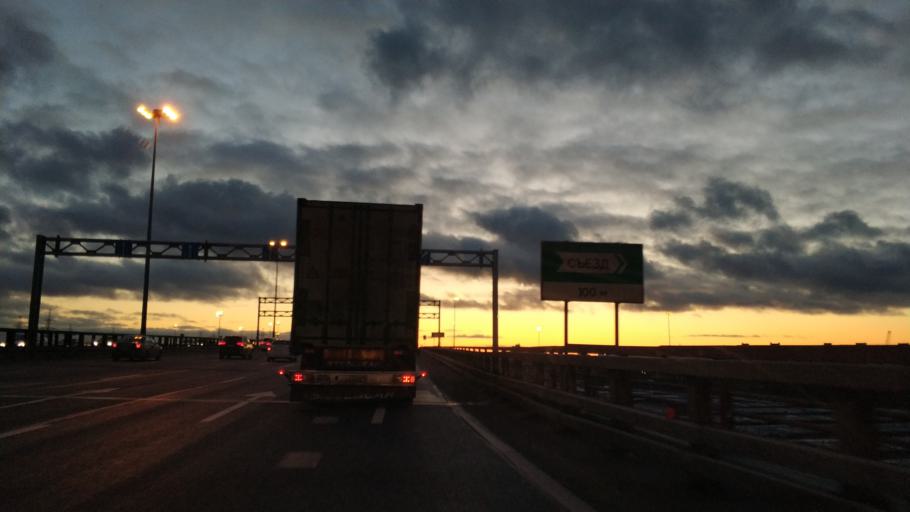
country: RU
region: St.-Petersburg
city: Obukhovo
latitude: 59.8355
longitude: 30.4486
